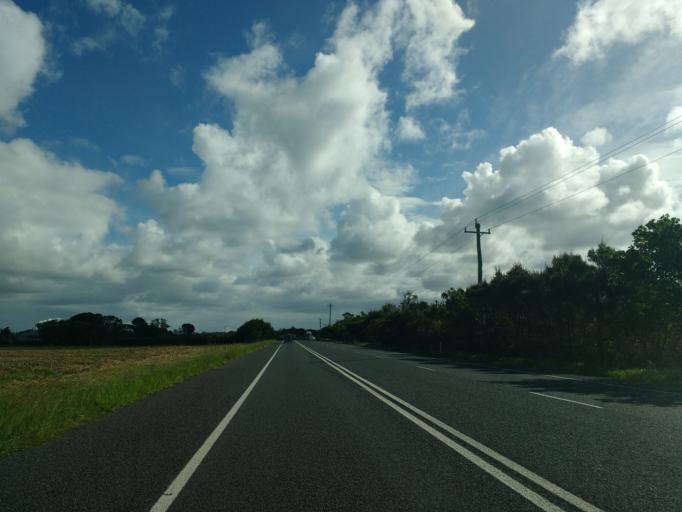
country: AU
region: New South Wales
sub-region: Richmond Valley
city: Evans Head
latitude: -28.9972
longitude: 153.4513
